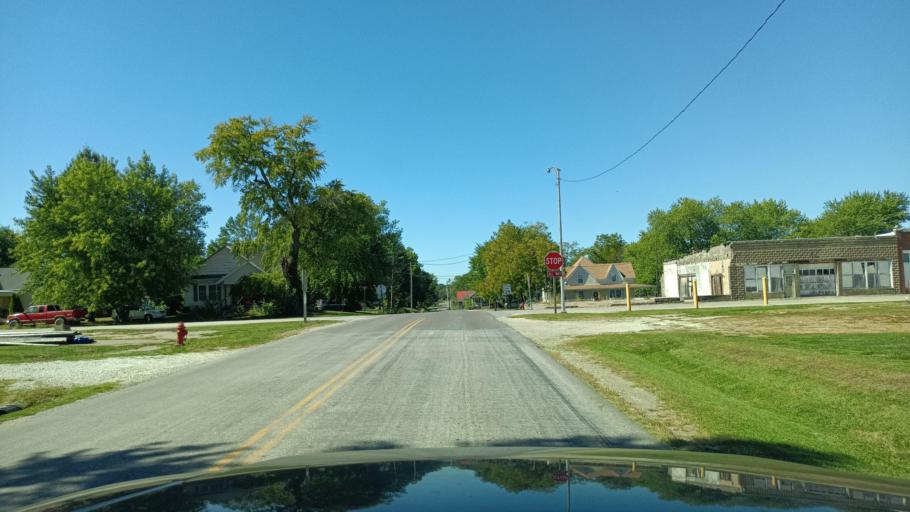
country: US
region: Missouri
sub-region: Macon County
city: La Plata
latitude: 40.0210
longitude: -92.4911
